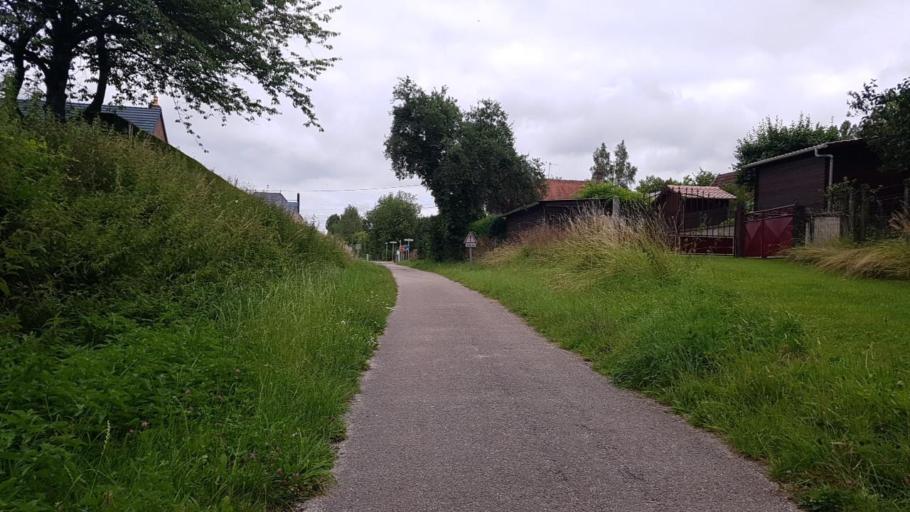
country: FR
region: Picardie
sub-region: Departement de l'Aisne
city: Origny-en-Thierache
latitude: 49.9310
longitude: 4.0225
